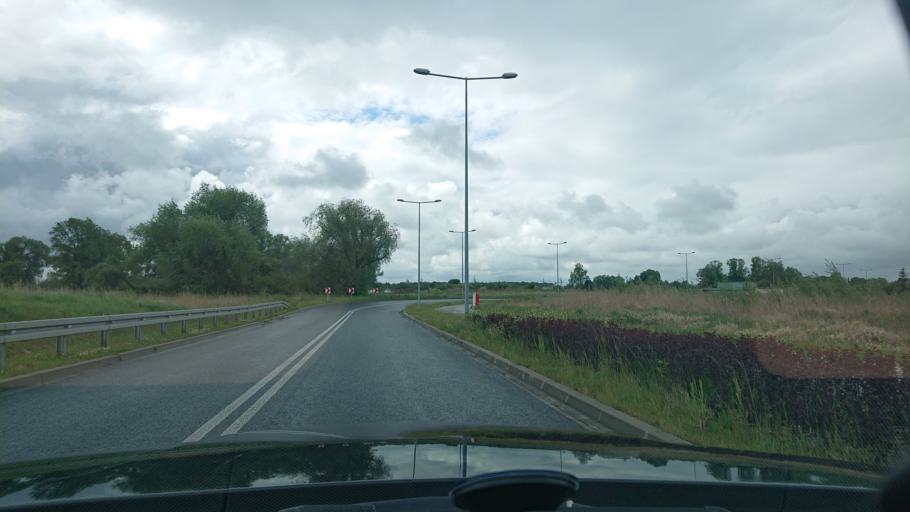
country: PL
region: Greater Poland Voivodeship
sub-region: Powiat gnieznienski
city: Gniezno
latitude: 52.5248
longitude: 17.6235
